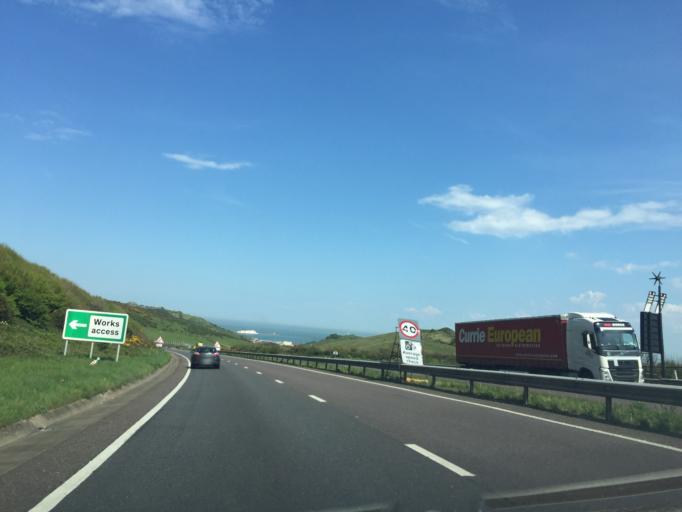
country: GB
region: England
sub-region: Kent
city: Dover
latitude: 51.1082
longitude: 1.2720
